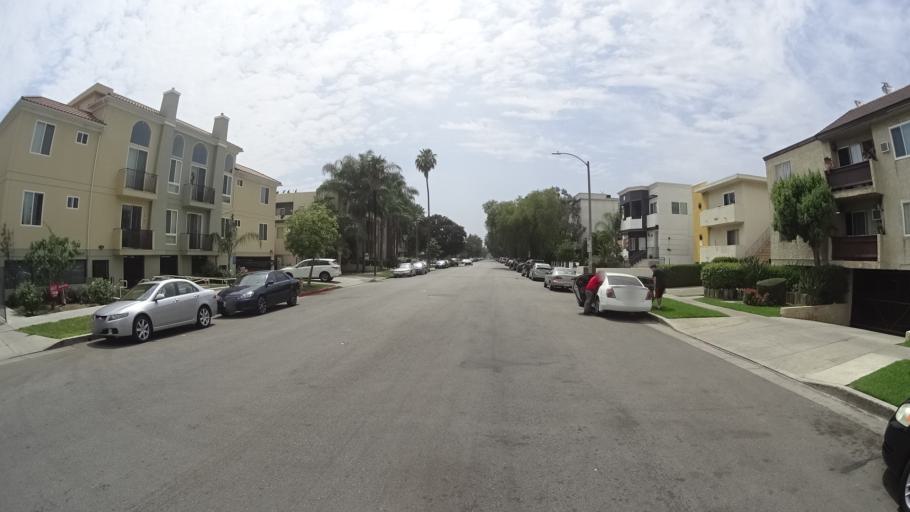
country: US
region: California
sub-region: Los Angeles County
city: Van Nuys
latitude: 34.1847
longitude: -118.4517
